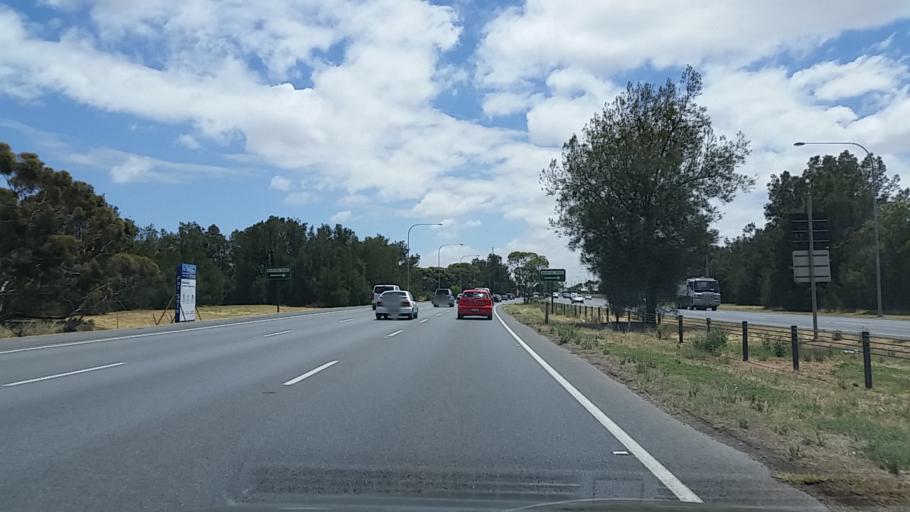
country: AU
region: South Australia
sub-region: Salisbury
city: Salisbury
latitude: -34.7982
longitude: 138.5964
